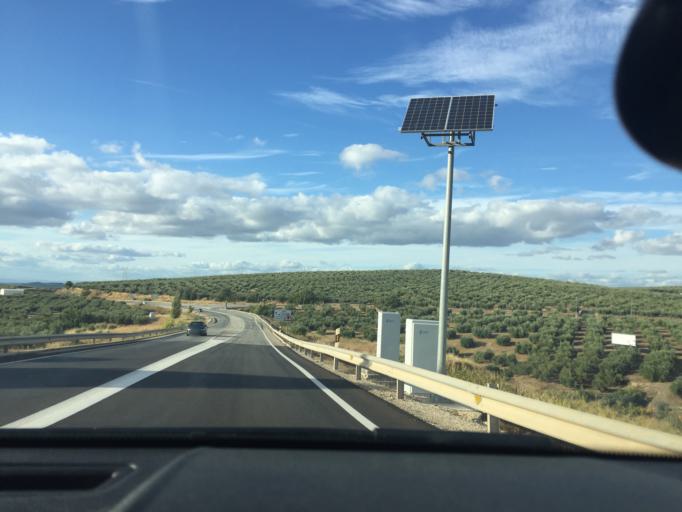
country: ES
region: Andalusia
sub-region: Provincia de Jaen
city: Torredonjimeno
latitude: 37.7671
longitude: -3.9701
